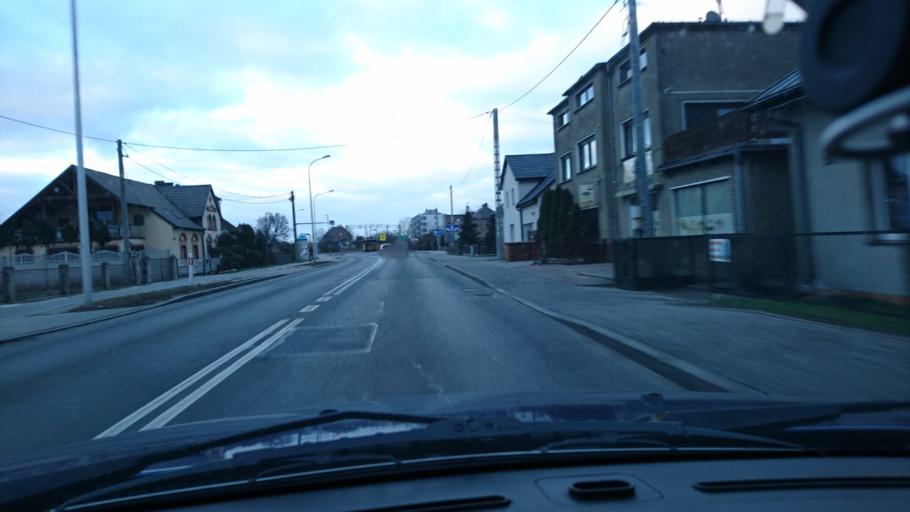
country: PL
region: Greater Poland Voivodeship
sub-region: Powiat kepinski
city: Kepno
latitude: 51.2963
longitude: 17.9969
